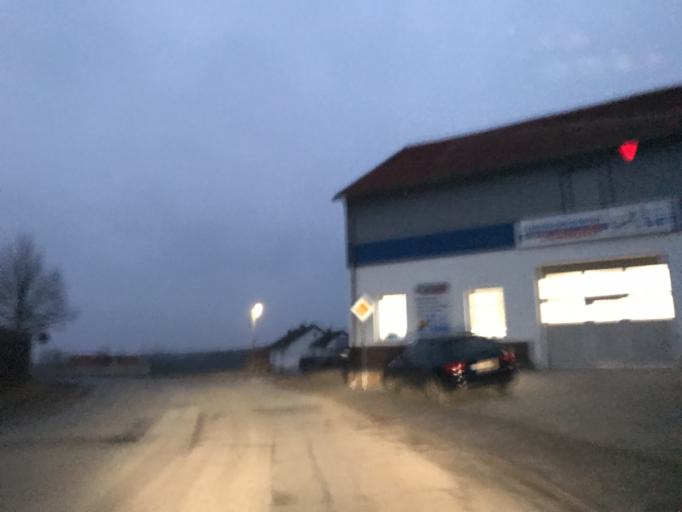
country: DE
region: Hesse
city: Trendelburg
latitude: 51.5741
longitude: 9.4162
